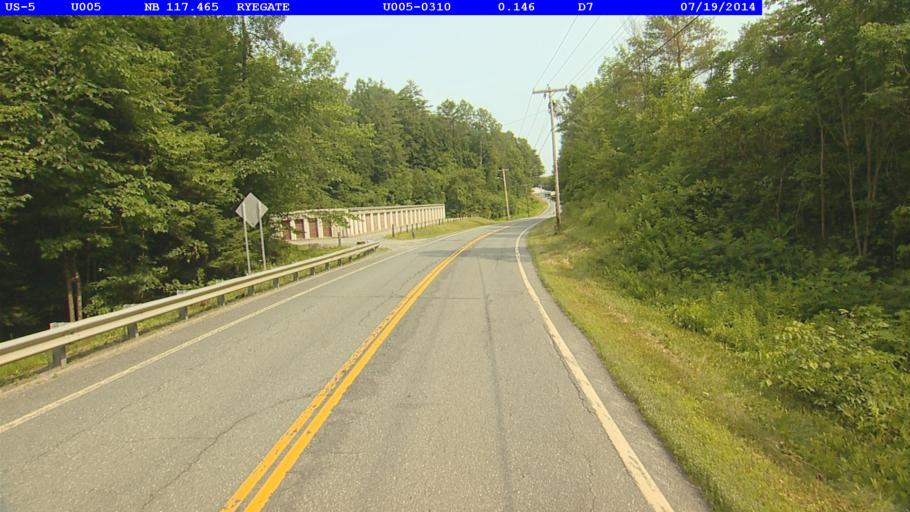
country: US
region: New Hampshire
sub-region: Grafton County
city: Woodsville
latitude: 44.1597
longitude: -72.0478
